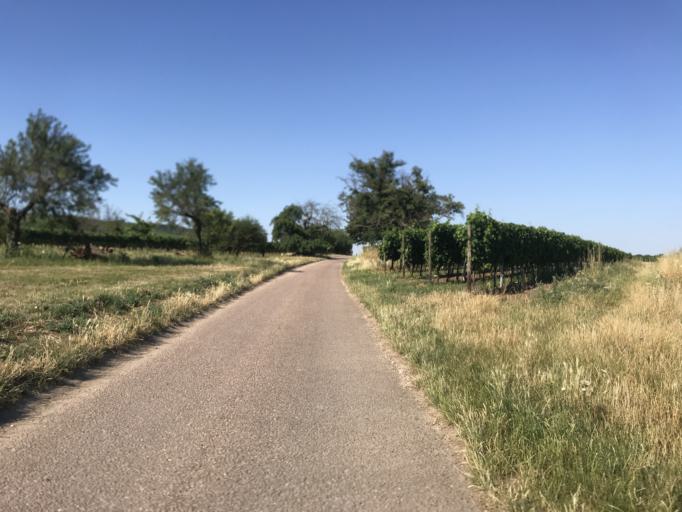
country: DE
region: Rheinland-Pfalz
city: Gau-Algesheim
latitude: 49.9551
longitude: 8.0112
